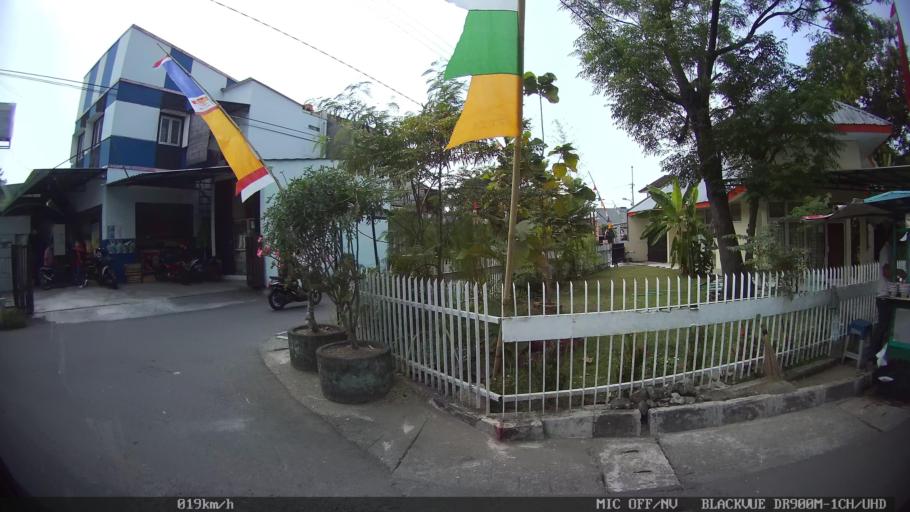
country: ID
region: Daerah Istimewa Yogyakarta
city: Yogyakarta
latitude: -7.7972
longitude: 110.3943
